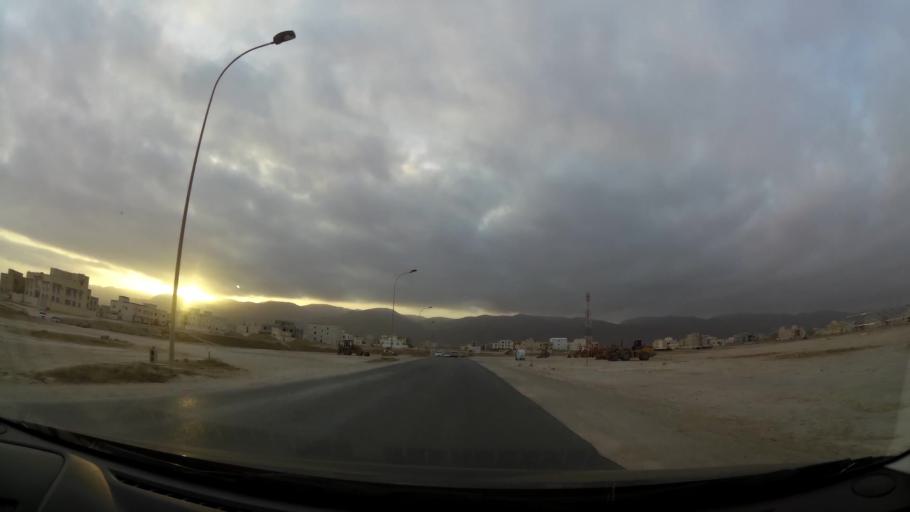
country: OM
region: Zufar
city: Salalah
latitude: 17.0356
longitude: 54.0269
